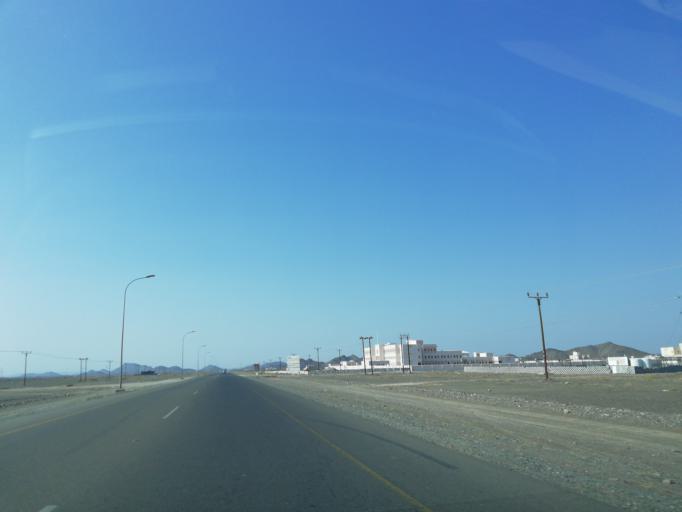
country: OM
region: Ash Sharqiyah
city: Ibra'
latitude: 22.7691
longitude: 58.1443
